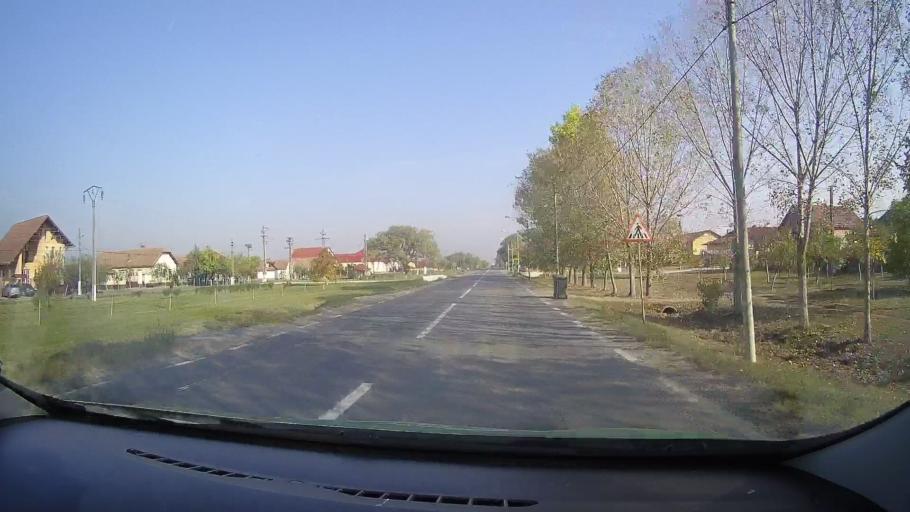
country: RO
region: Arad
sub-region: Comuna Pilu
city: Pilu
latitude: 46.5746
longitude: 21.3425
